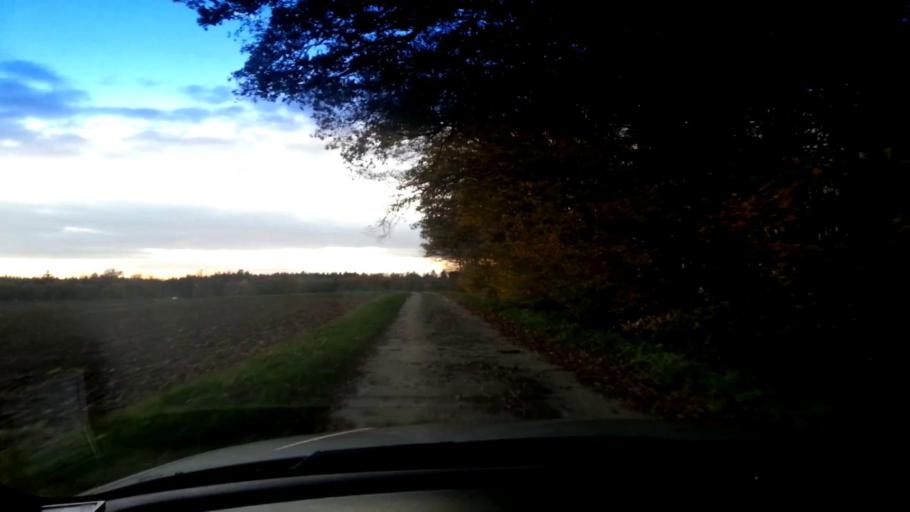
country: DE
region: Bavaria
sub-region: Upper Franconia
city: Litzendorf
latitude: 49.9222
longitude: 10.9896
